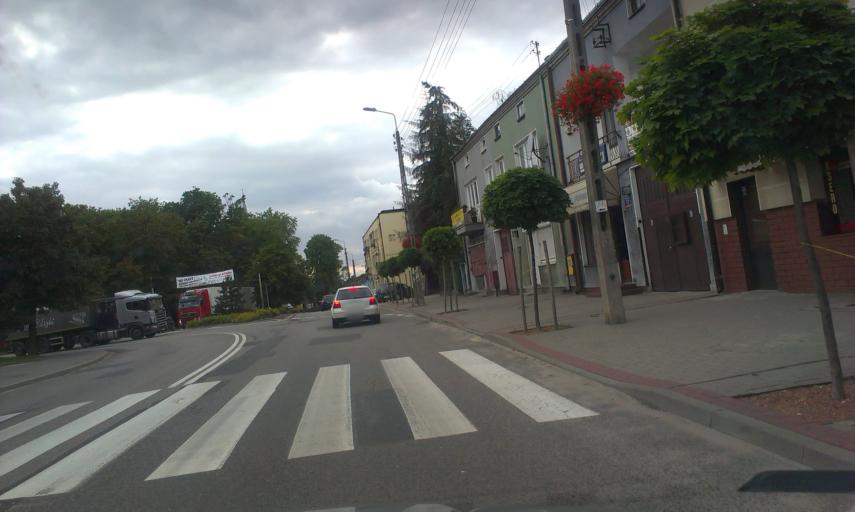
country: PL
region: Masovian Voivodeship
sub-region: Powiat zyrardowski
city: Mszczonow
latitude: 51.9744
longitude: 20.5136
